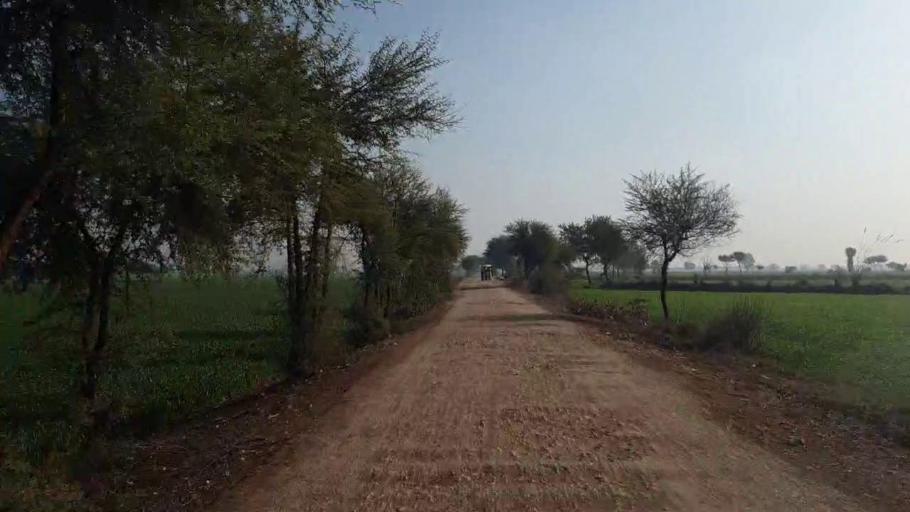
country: PK
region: Sindh
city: Shahdadpur
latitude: 26.0003
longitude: 68.6205
